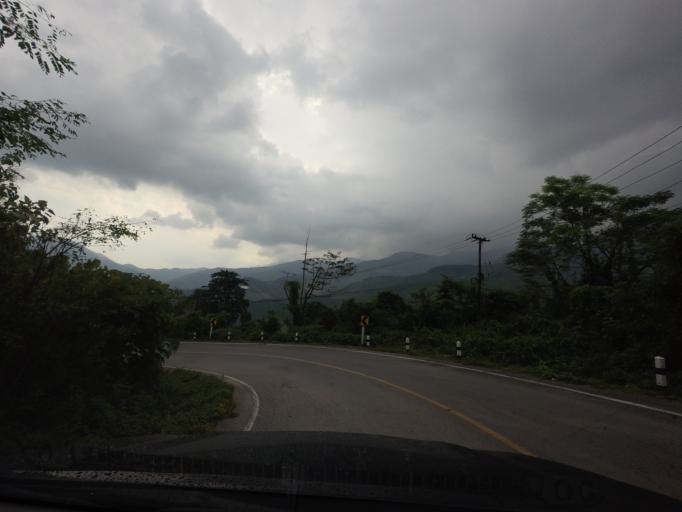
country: TH
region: Nan
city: Bo Kluea
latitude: 19.1634
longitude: 101.1409
